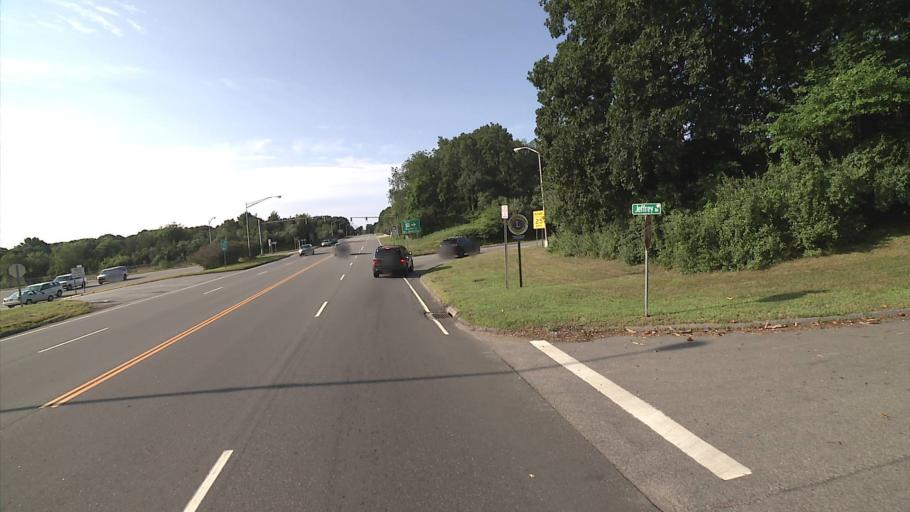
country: US
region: Connecticut
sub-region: New London County
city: Pawcatuck
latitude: 41.3950
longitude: -71.8454
